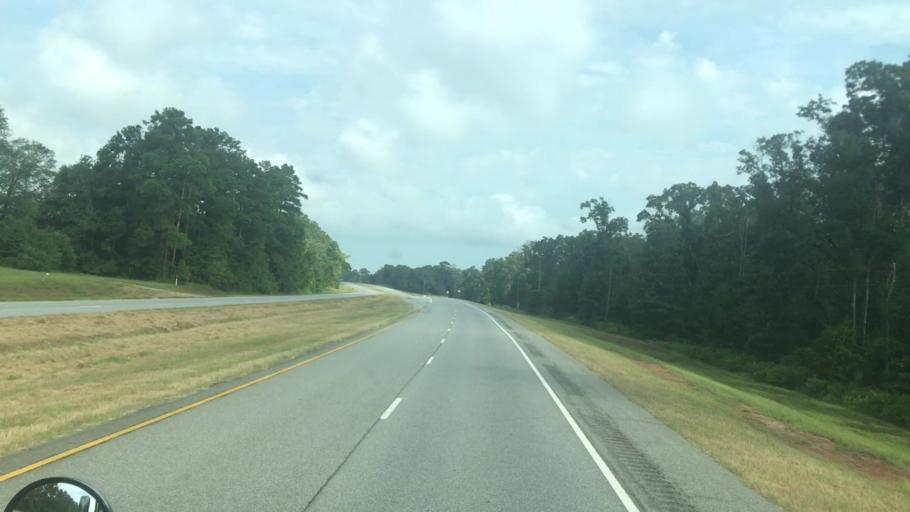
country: US
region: Georgia
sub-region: Miller County
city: Colquitt
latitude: 31.2440
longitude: -84.7906
